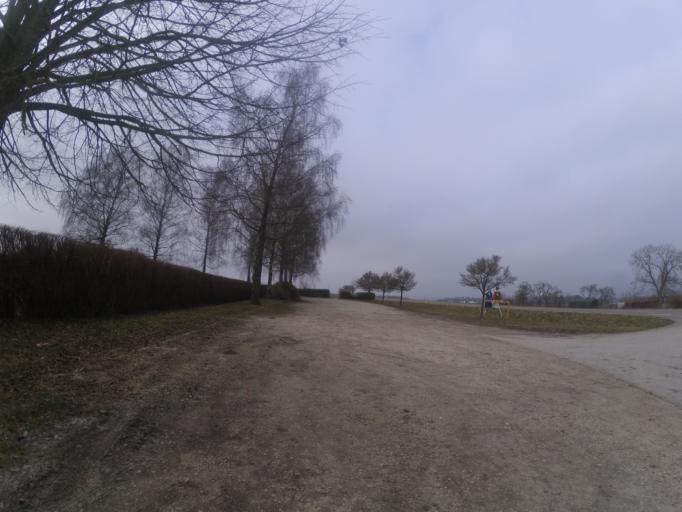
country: DE
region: Baden-Wuerttemberg
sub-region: Tuebingen Region
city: Munderkingen
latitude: 48.2401
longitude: 9.6306
